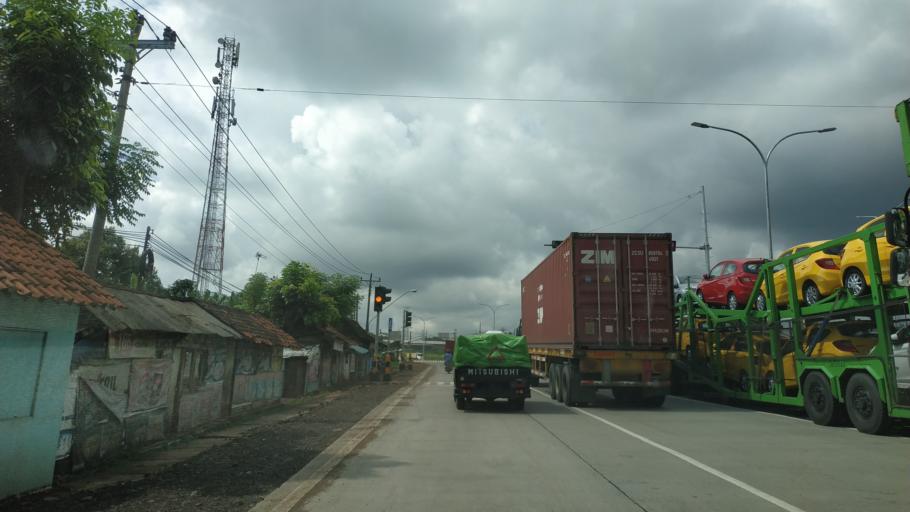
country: ID
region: Central Java
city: Pekalongan
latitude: -6.9314
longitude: 109.7647
